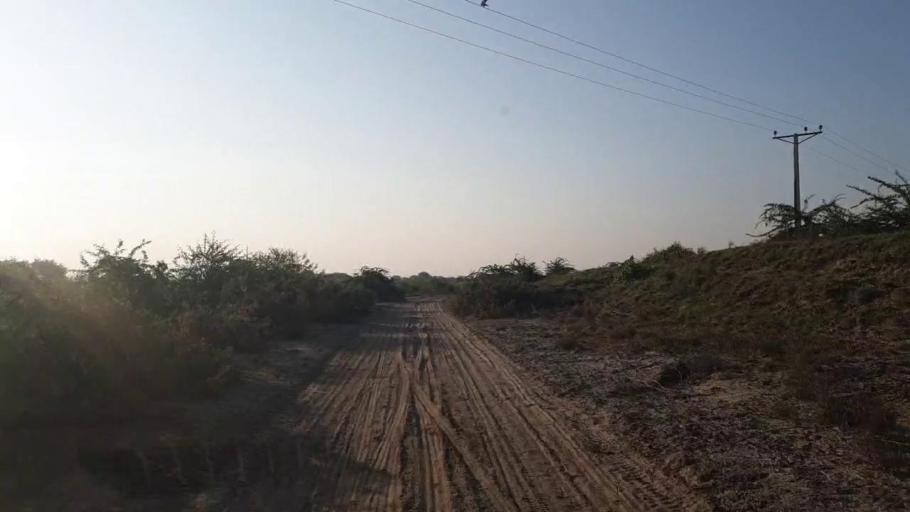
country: PK
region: Sindh
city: Badin
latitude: 24.6312
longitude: 68.7956
